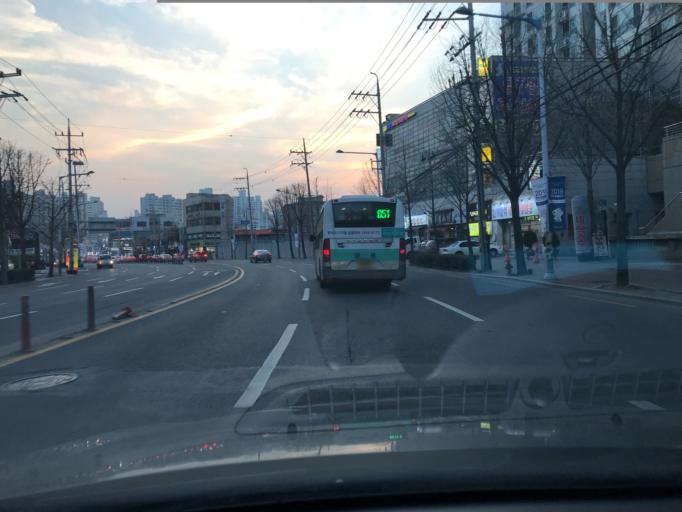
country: KR
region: Daegu
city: Hwawon
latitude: 35.8134
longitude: 128.5198
